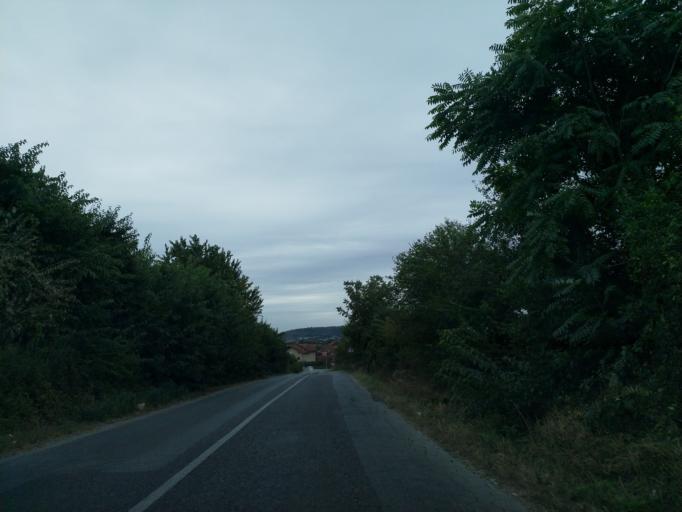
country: RS
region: Central Serbia
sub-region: Pomoravski Okrug
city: Jagodina
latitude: 43.9887
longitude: 21.2352
